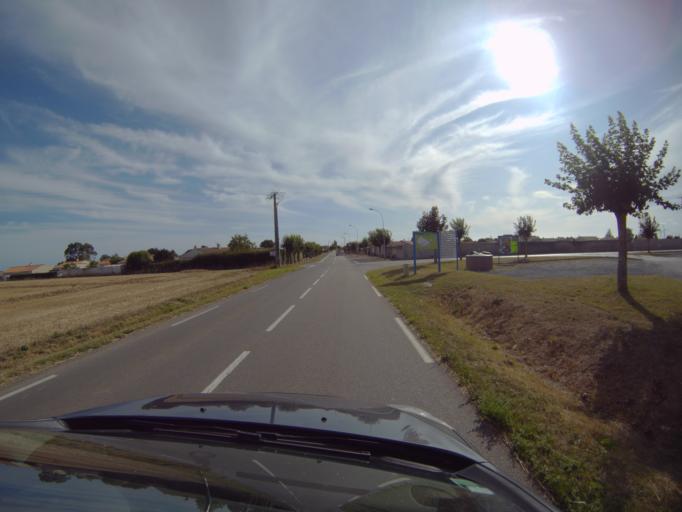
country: FR
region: Pays de la Loire
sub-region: Departement de la Vendee
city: Angles
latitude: 46.4128
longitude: -1.3930
